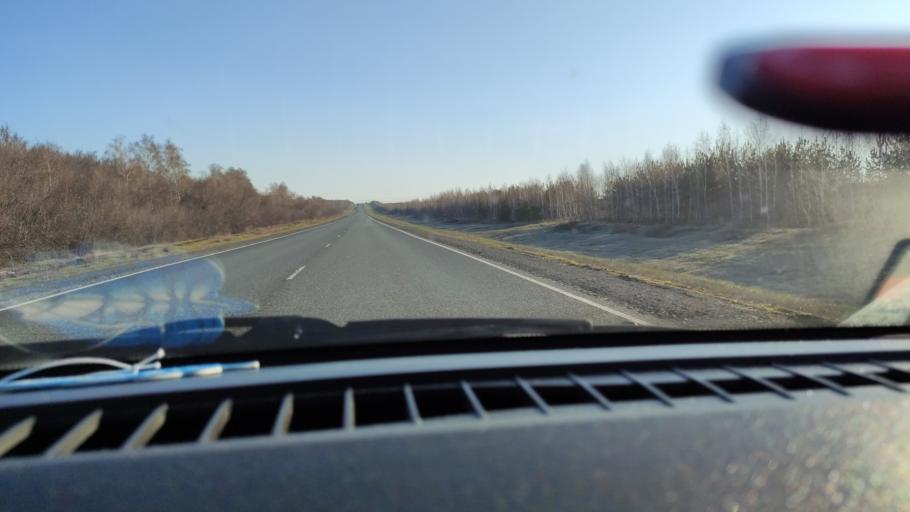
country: RU
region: Saratov
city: Balakovo
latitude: 52.1457
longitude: 47.8059
